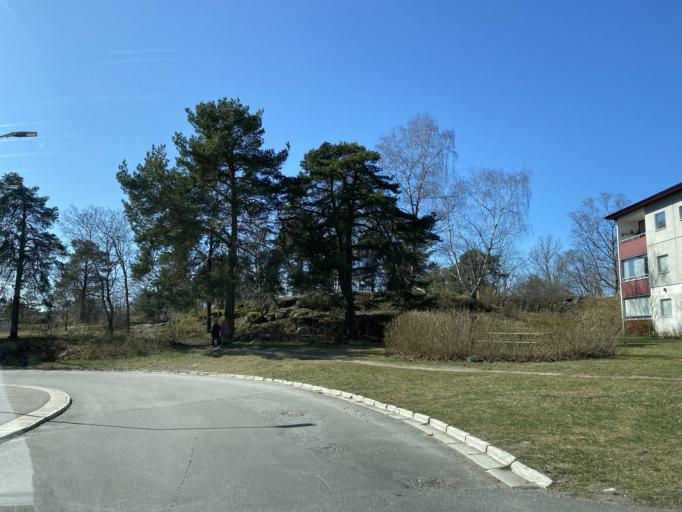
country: SE
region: Stockholm
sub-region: Stockholms Kommun
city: Arsta
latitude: 59.2854
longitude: 18.0373
